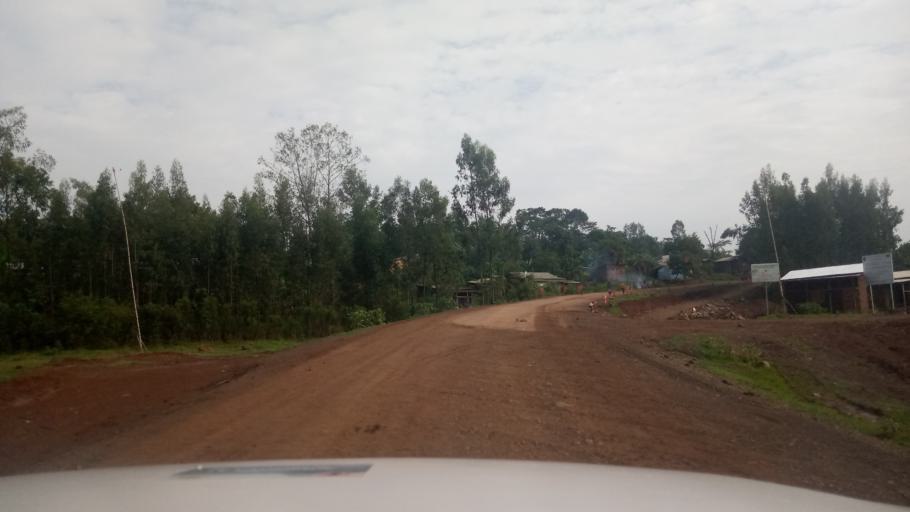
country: ET
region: Oromiya
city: Agaro
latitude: 7.8576
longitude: 36.6520
